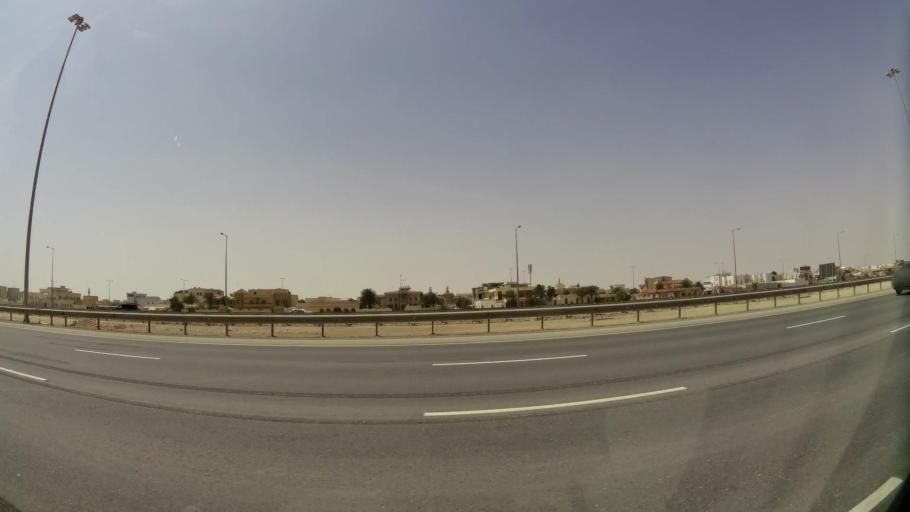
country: QA
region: Baladiyat Umm Salal
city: Umm Salal Muhammad
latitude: 25.3924
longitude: 51.4341
